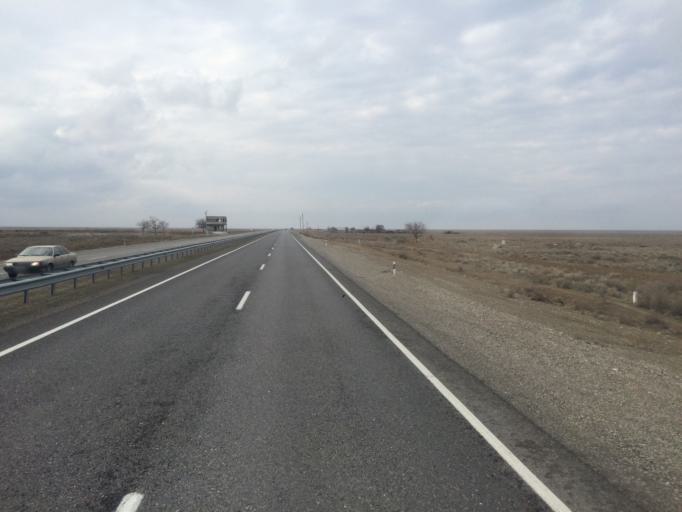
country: KZ
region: Ongtustik Qazaqstan
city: Turkestan
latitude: 43.5253
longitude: 67.7947
